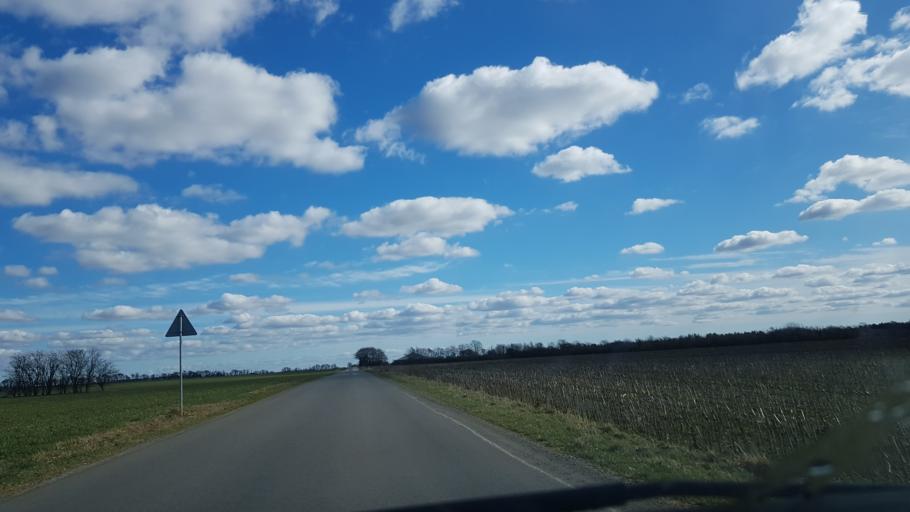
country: DK
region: South Denmark
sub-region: Vejen Kommune
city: Rodding
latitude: 55.3960
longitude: 9.0129
